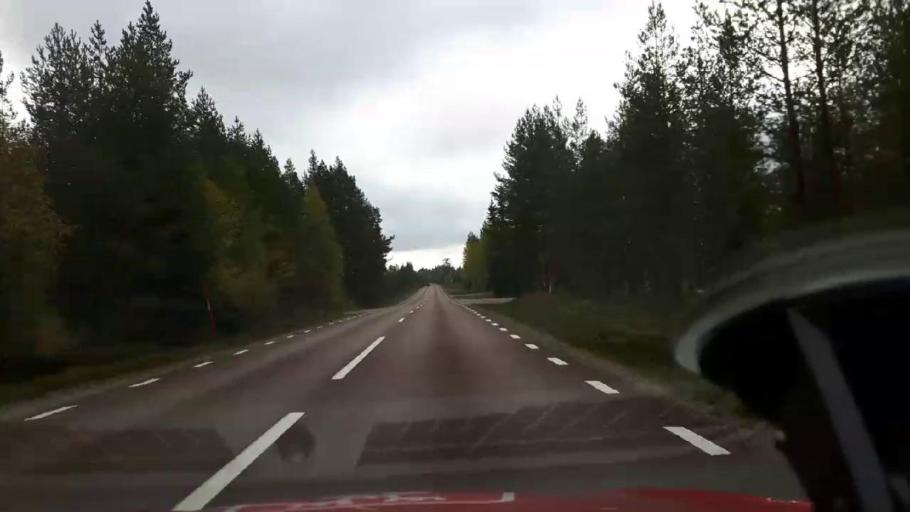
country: SE
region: Jaemtland
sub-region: Harjedalens Kommun
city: Sveg
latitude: 62.1863
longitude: 14.8667
